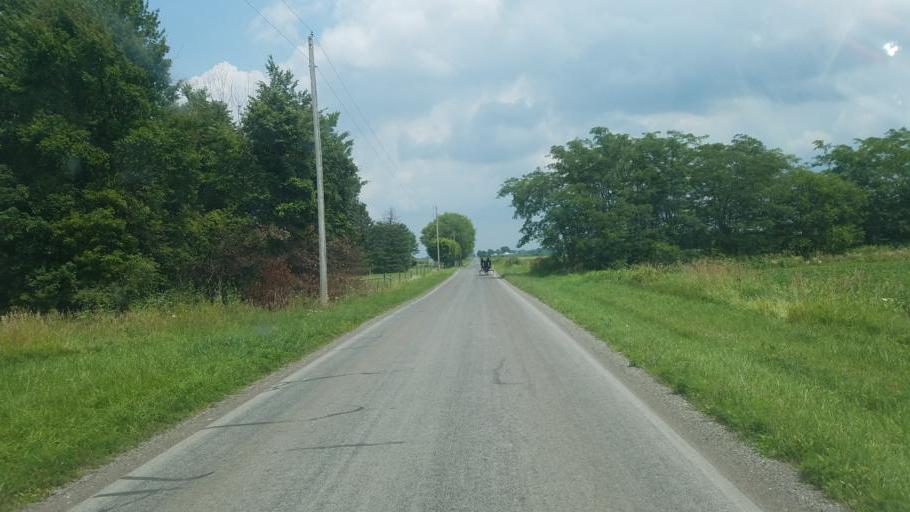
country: US
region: Ohio
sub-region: Hardin County
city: Kenton
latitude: 40.5943
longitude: -83.6122
